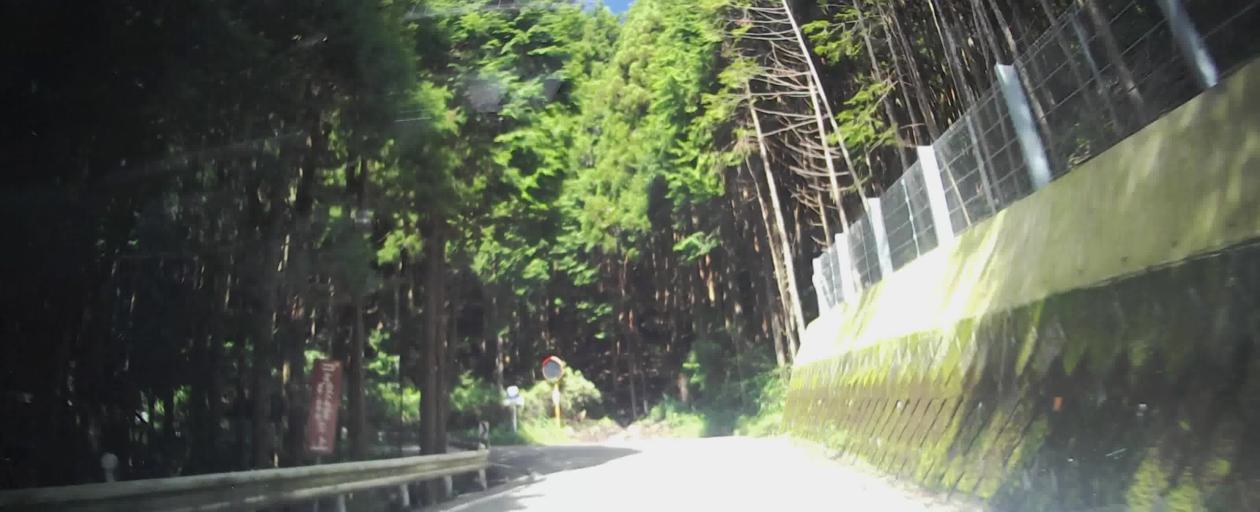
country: JP
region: Gunma
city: Shibukawa
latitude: 36.4536
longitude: 138.8994
